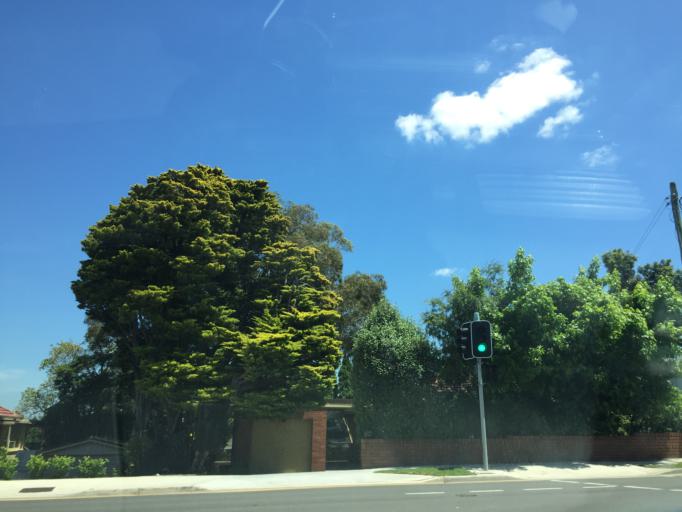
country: AU
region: New South Wales
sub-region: Parramatta
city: Dundas Valley
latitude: -33.7871
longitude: 151.0613
